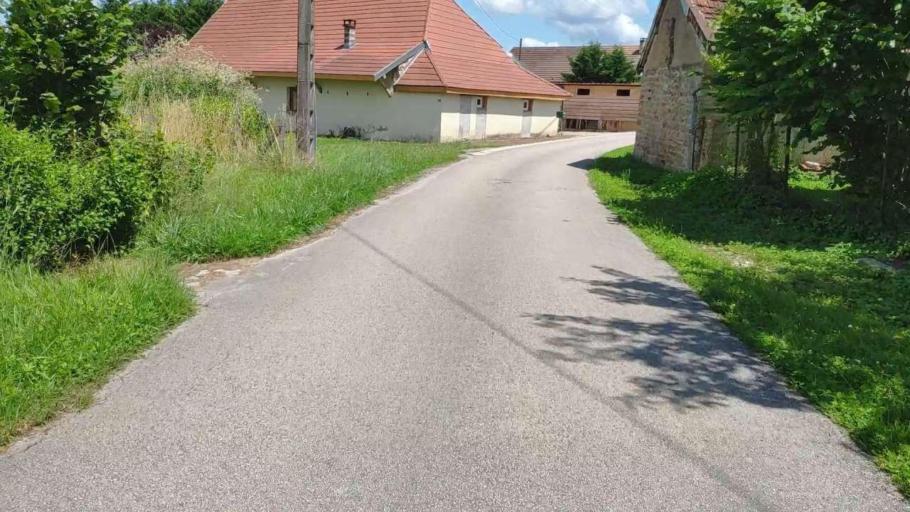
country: FR
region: Franche-Comte
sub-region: Departement du Jura
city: Chaussin
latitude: 46.8764
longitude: 5.4850
